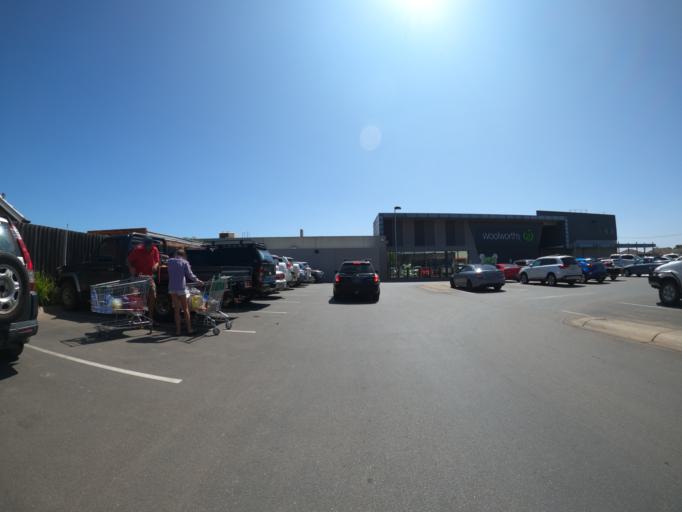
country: AU
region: Victoria
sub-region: Moira
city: Yarrawonga
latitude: -36.0158
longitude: 146.0041
